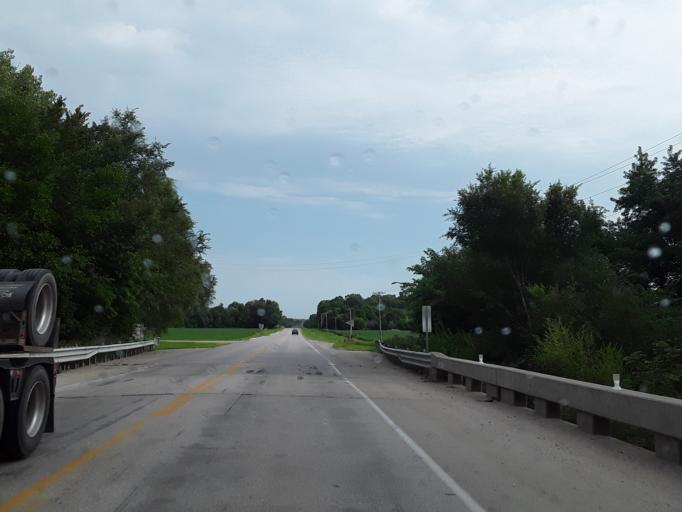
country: US
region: Nebraska
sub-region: Saunders County
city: Ashland
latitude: 41.0586
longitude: -96.3680
